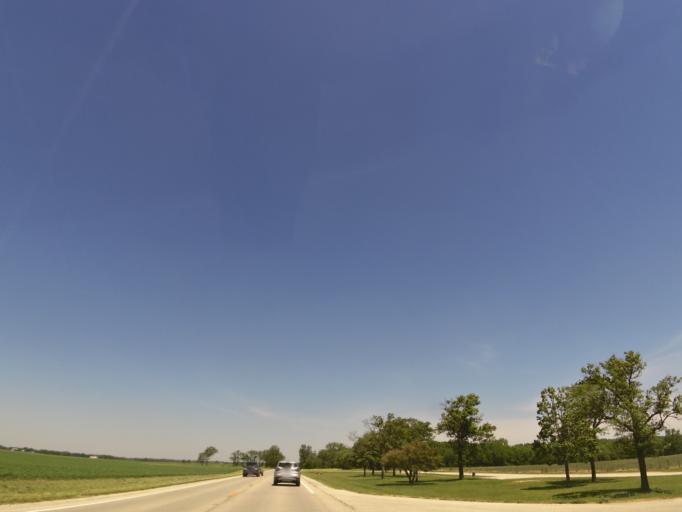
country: US
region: Illinois
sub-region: Iroquois County
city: Milford
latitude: 40.5653
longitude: -87.6937
